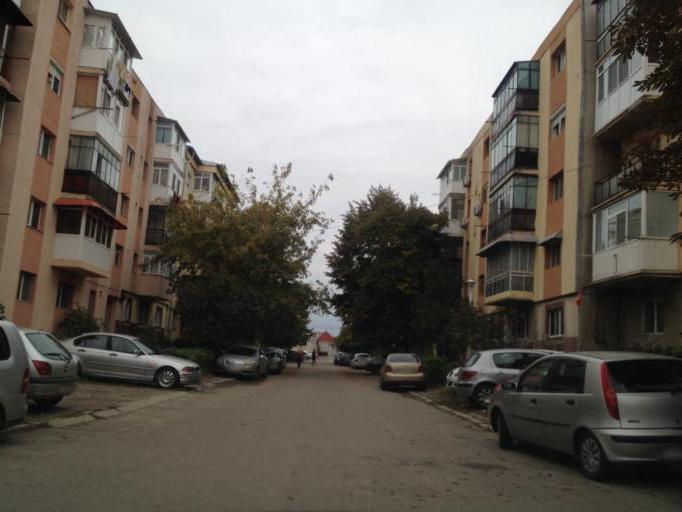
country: RO
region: Dolj
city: Craiova
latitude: 44.3341
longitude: 23.7782
